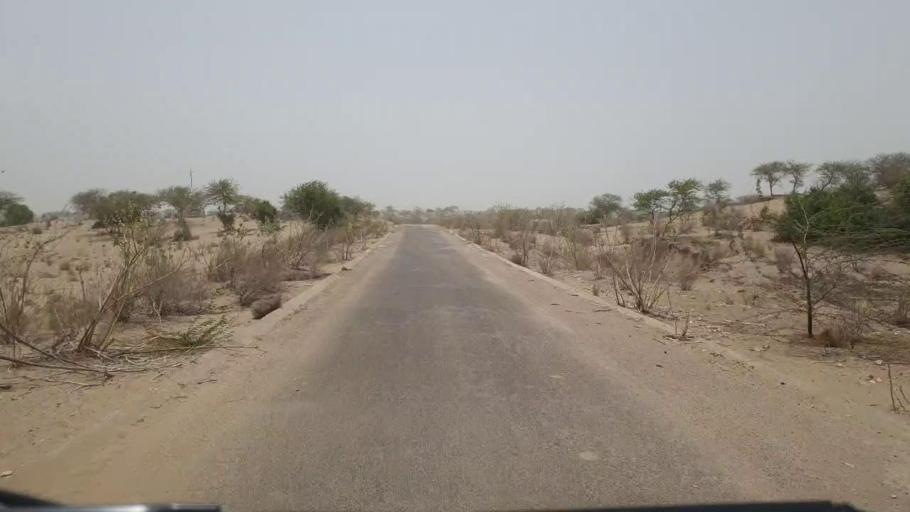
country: PK
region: Sindh
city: Naukot
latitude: 24.7668
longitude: 69.5401
